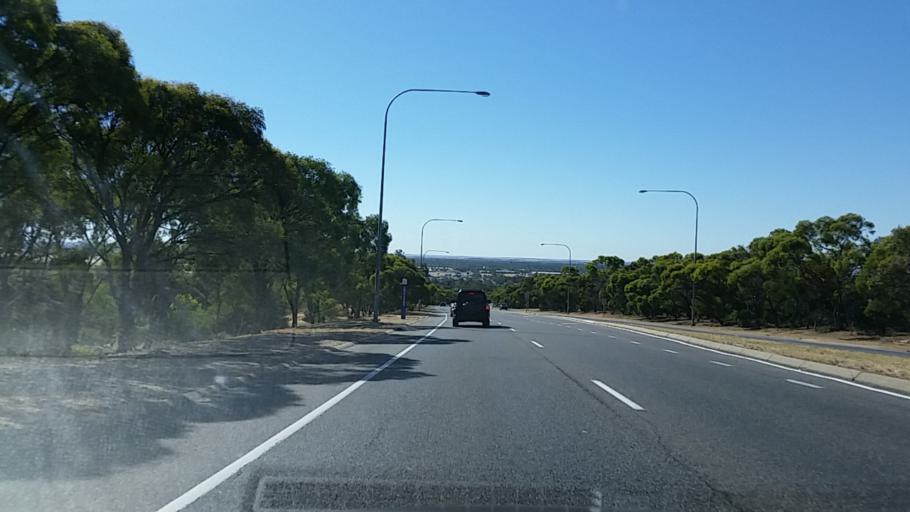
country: AU
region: South Australia
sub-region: Tea Tree Gully
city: Modbury
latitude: -34.8057
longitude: 138.6664
